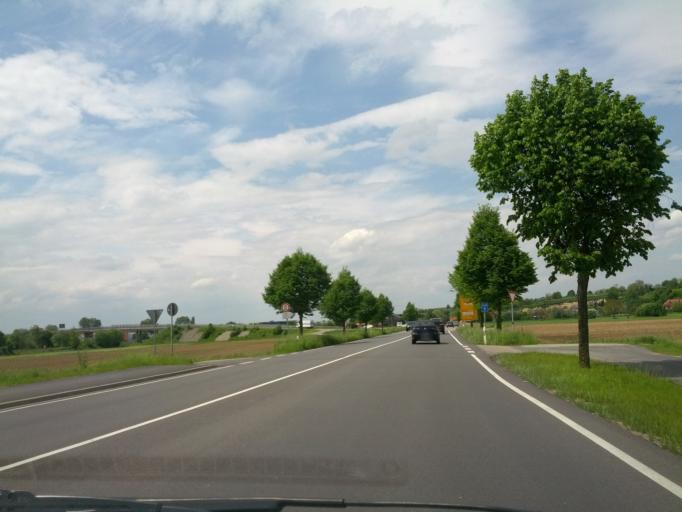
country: DE
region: Baden-Wuerttemberg
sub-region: Freiburg Region
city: Teningen
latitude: 48.1314
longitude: 7.8207
